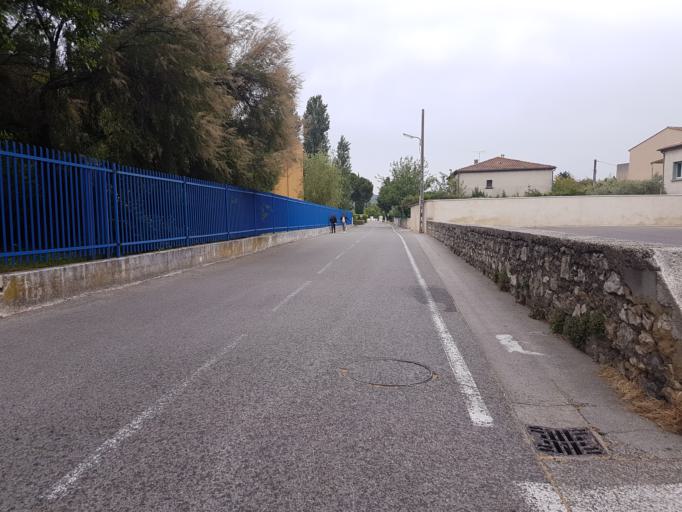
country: FR
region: Languedoc-Roussillon
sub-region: Departement du Gard
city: Roquemaure
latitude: 44.0487
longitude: 4.7793
